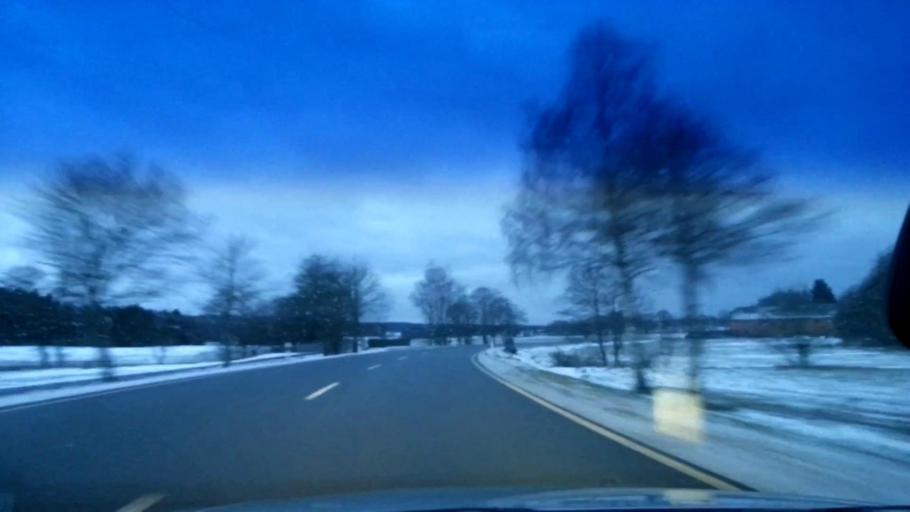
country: DE
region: Bavaria
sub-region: Upper Franconia
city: Weissenstadt
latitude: 50.0944
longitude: 11.8665
